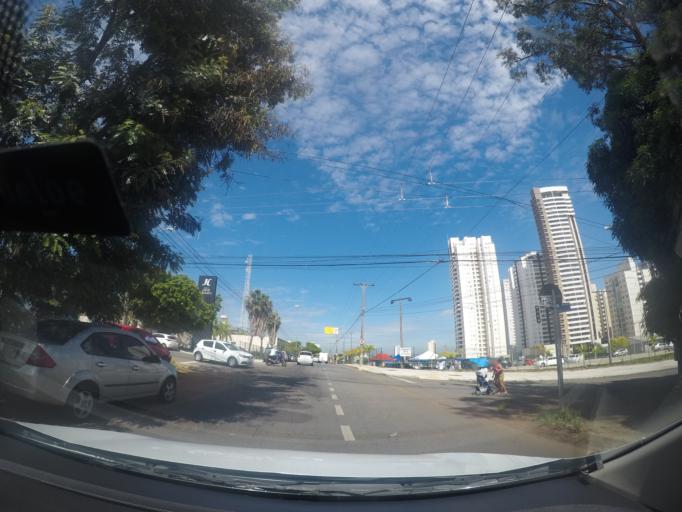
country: BR
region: Goias
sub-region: Goiania
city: Goiania
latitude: -16.7218
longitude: -49.2641
